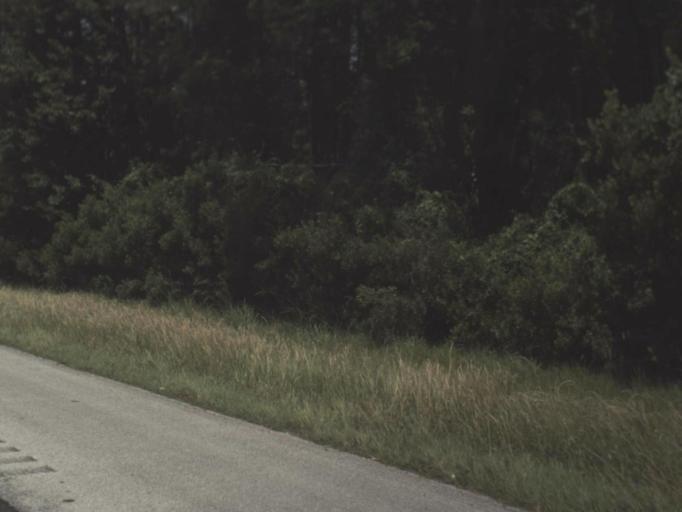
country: US
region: Florida
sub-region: Duval County
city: Baldwin
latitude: 30.2853
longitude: -82.0285
